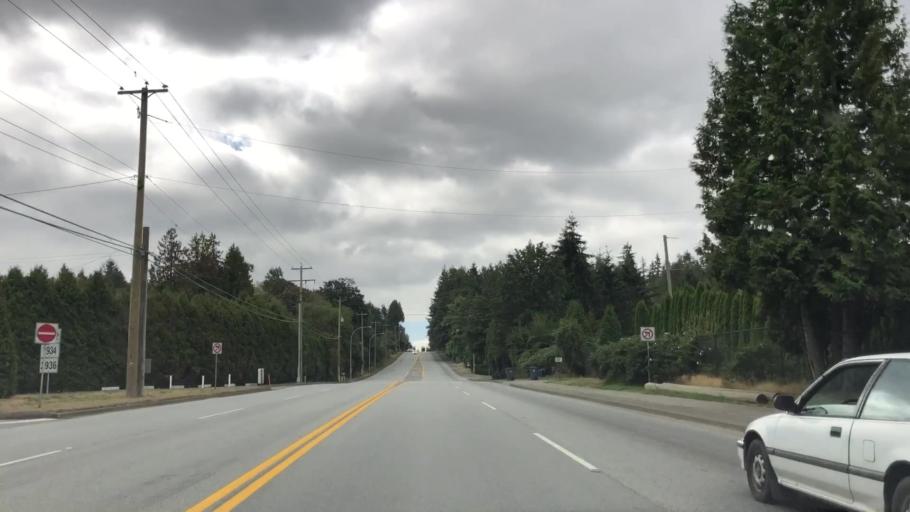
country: US
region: Washington
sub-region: Whatcom County
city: Blaine
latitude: 49.0553
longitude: -122.7354
